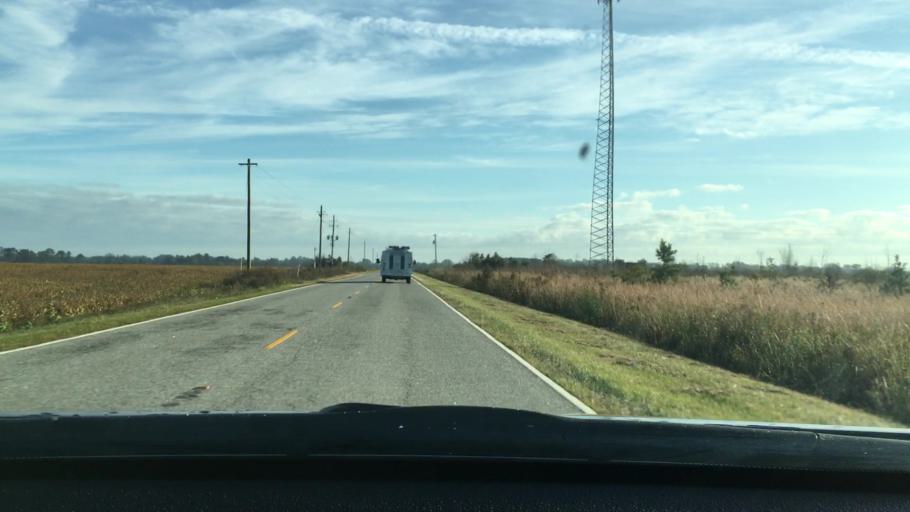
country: US
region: South Carolina
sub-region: Sumter County
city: East Sumter
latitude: 34.0562
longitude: -80.2372
